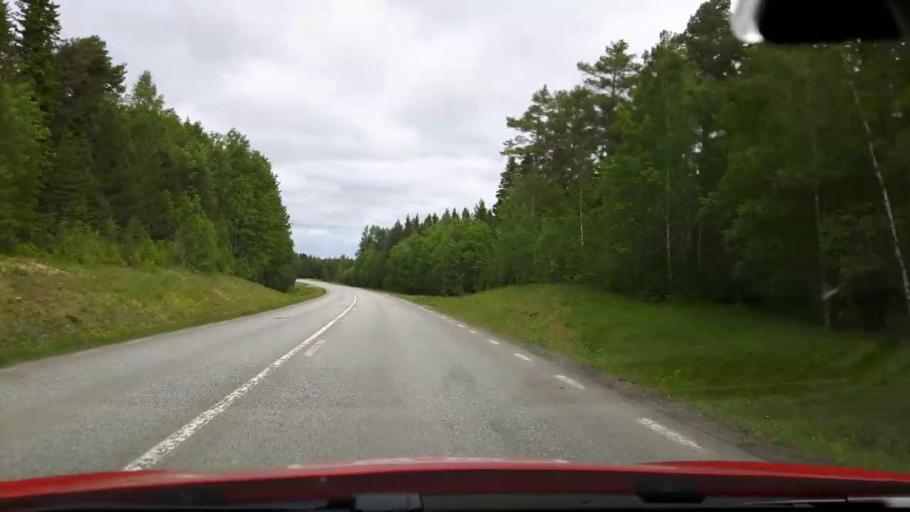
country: SE
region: Jaemtland
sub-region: Krokoms Kommun
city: Krokom
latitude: 63.3660
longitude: 14.5071
